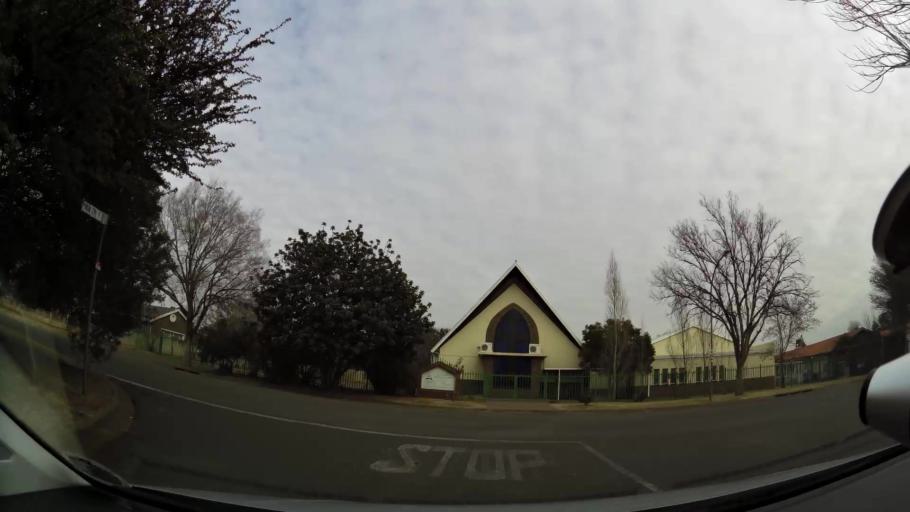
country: ZA
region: Orange Free State
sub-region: Mangaung Metropolitan Municipality
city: Bloemfontein
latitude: -29.1255
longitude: 26.1745
